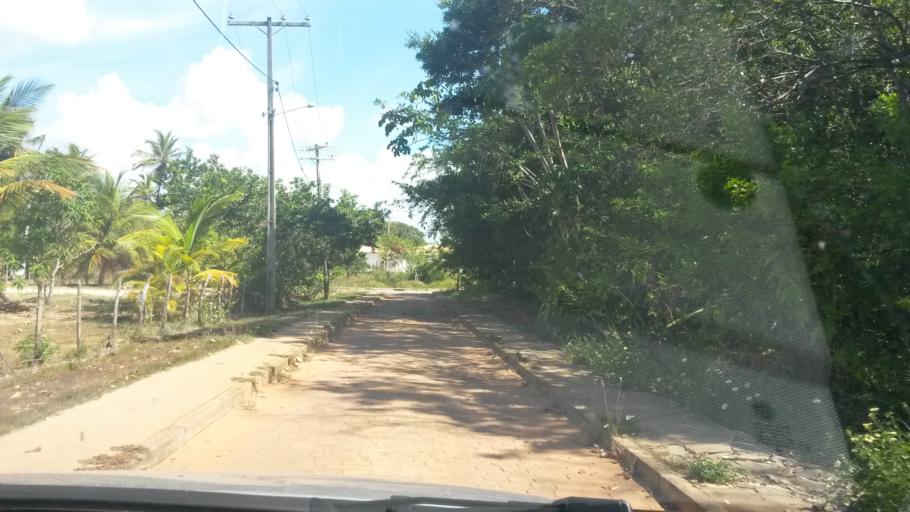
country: BR
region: Bahia
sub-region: Mata De Sao Joao
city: Mata de Sao Joao
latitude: -12.4897
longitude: -37.9577
